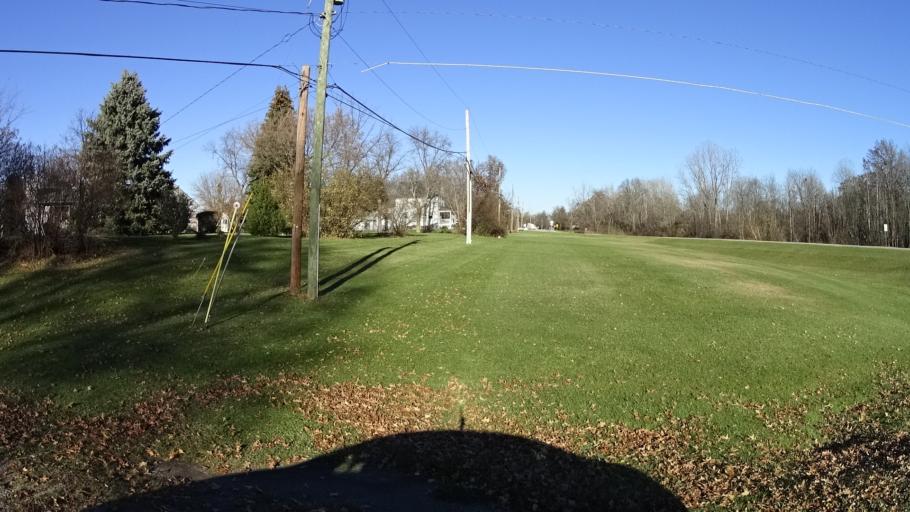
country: US
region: Ohio
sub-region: Lorain County
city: Elyria
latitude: 41.3325
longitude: -82.1281
